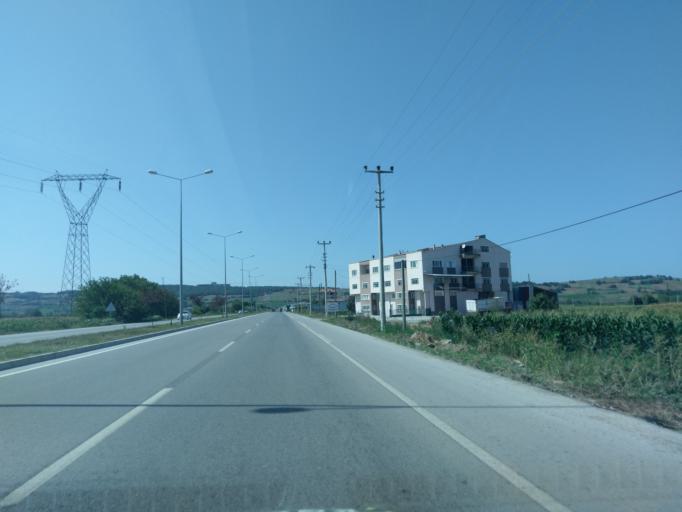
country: TR
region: Samsun
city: Bafra
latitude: 41.5757
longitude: 35.8595
